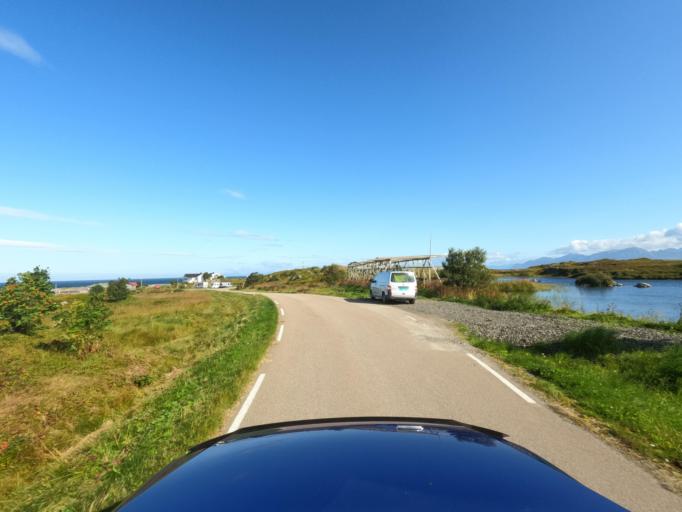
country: NO
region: Nordland
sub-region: Vestvagoy
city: Evjen
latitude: 68.3406
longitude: 14.0857
